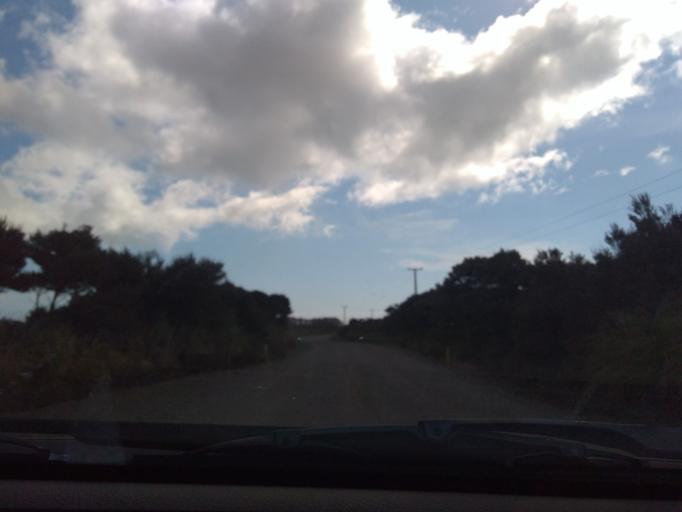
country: NZ
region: Northland
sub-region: Far North District
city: Taipa
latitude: -34.9511
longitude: 173.3742
